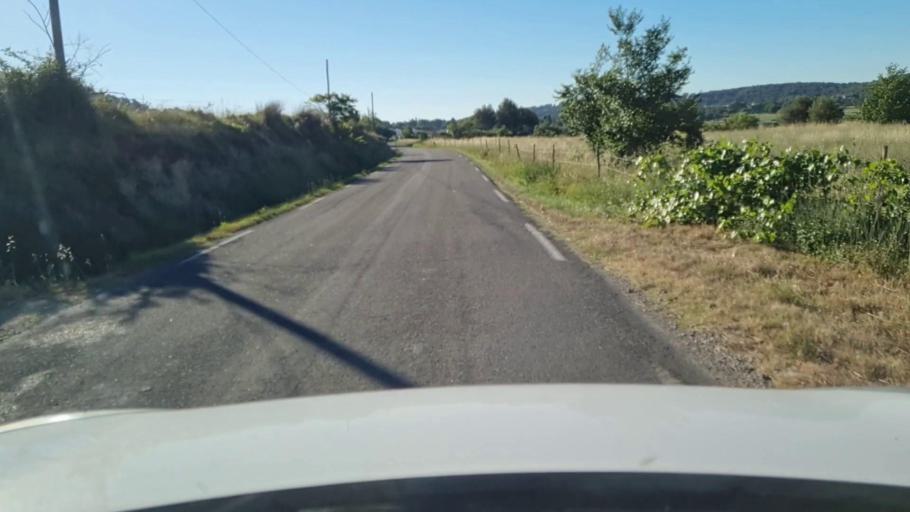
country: FR
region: Languedoc-Roussillon
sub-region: Departement du Gard
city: Caveirac
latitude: 43.8297
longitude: 4.2468
